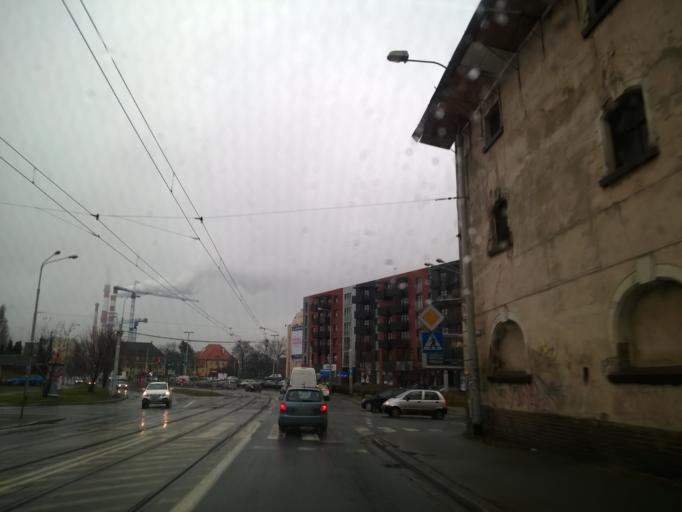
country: PL
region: Lower Silesian Voivodeship
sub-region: Powiat wroclawski
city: Wroclaw
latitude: 51.1153
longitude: 17.0245
